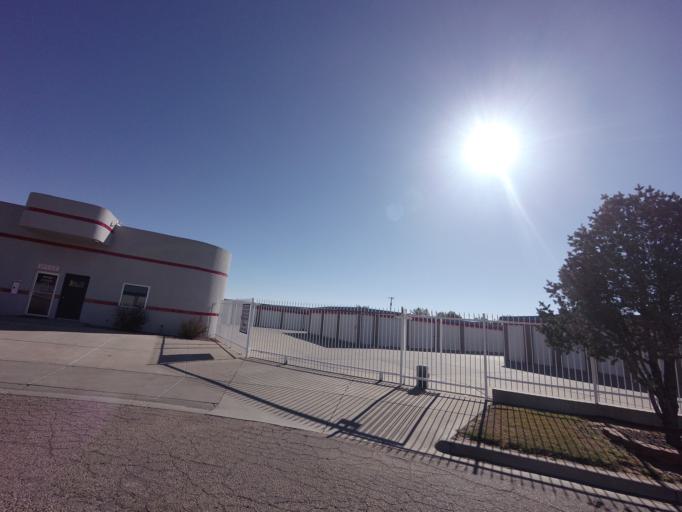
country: US
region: New Mexico
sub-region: Curry County
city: Clovis
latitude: 34.4329
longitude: -103.2010
